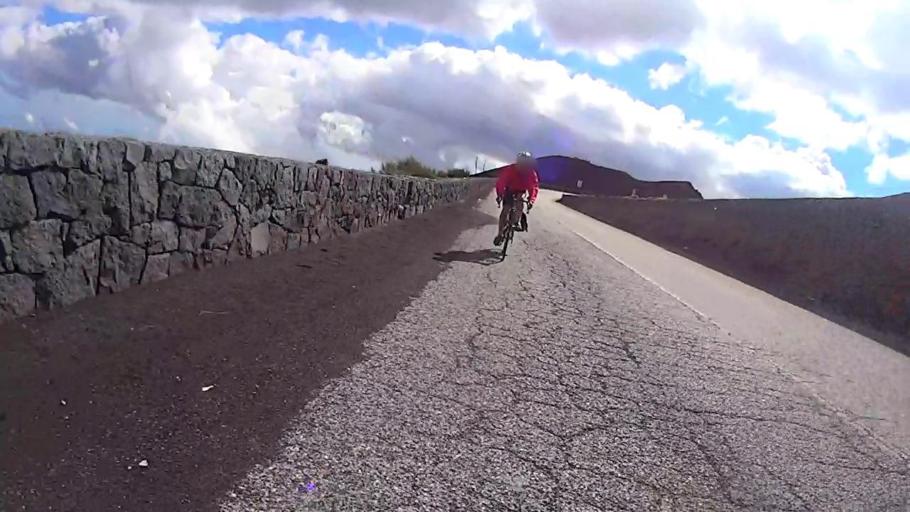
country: IT
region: Sicily
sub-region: Catania
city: Nicolosi
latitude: 37.6998
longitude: 15.0085
